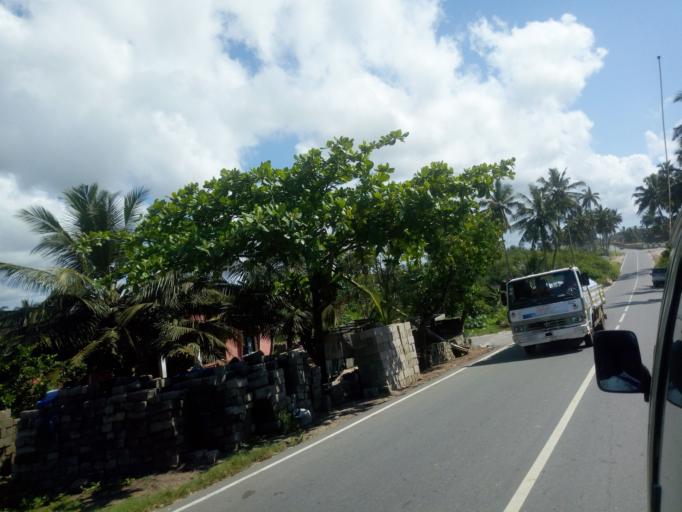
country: GH
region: Central
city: Elmina
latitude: 5.0918
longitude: -1.3433
